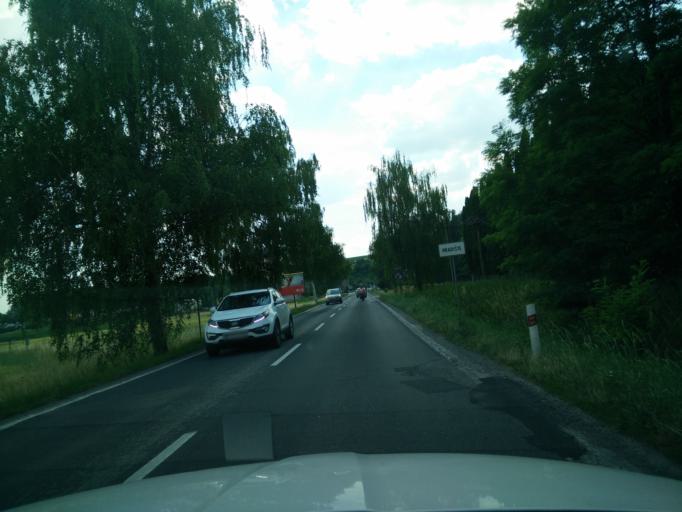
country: SK
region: Nitriansky
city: Partizanske
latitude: 48.6917
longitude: 18.3798
